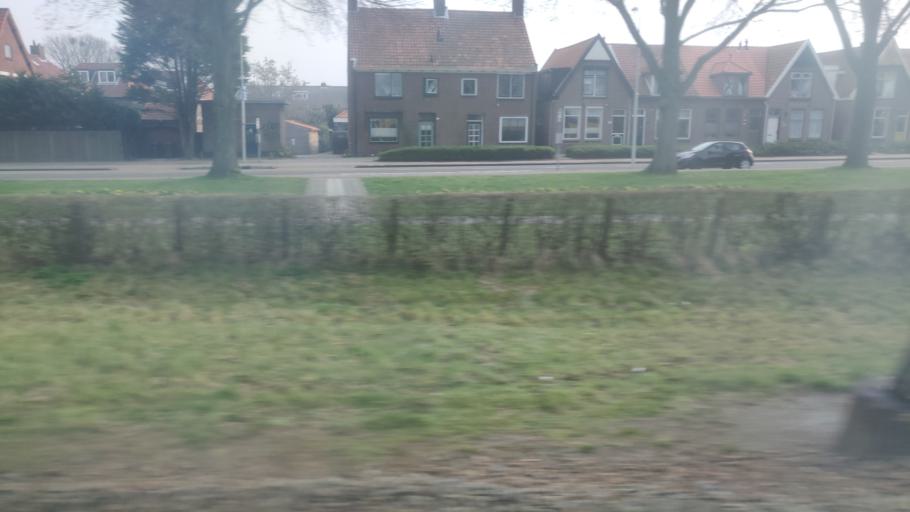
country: NL
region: North Holland
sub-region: Gemeente Castricum
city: Castricum
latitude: 52.5517
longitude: 4.6576
